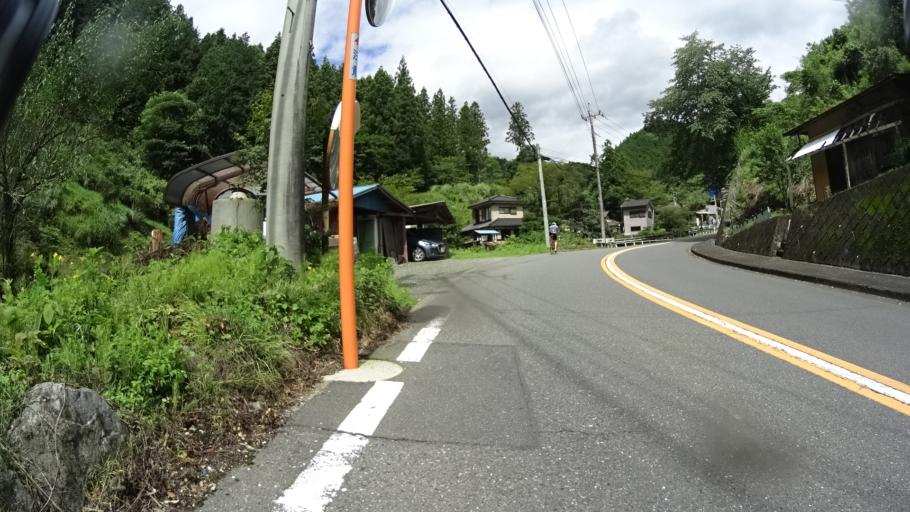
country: JP
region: Tokyo
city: Ome
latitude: 35.8362
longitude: 139.2041
